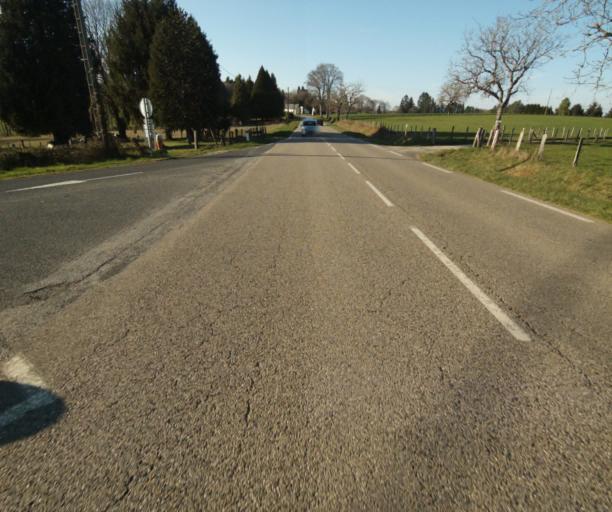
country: FR
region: Limousin
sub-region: Departement de la Correze
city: Seilhac
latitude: 45.3781
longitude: 1.7235
